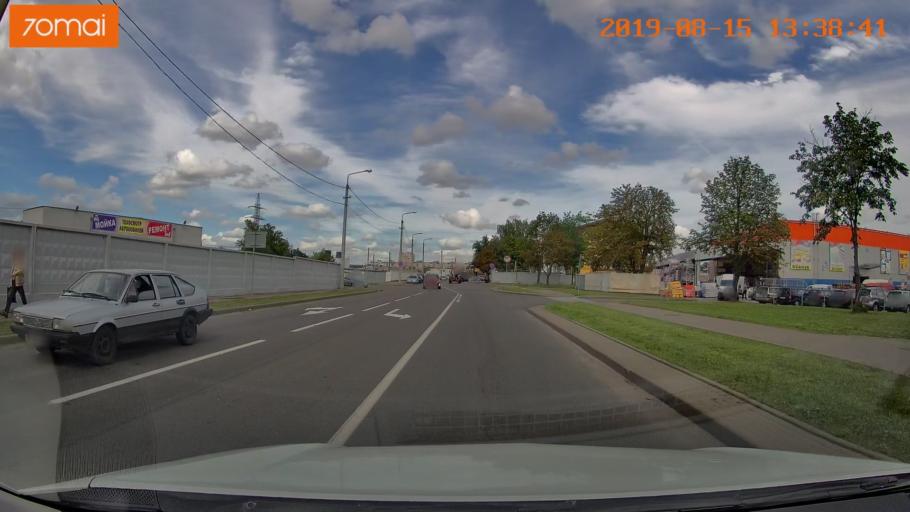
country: BY
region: Minsk
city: Minsk
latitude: 53.8765
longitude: 27.5933
